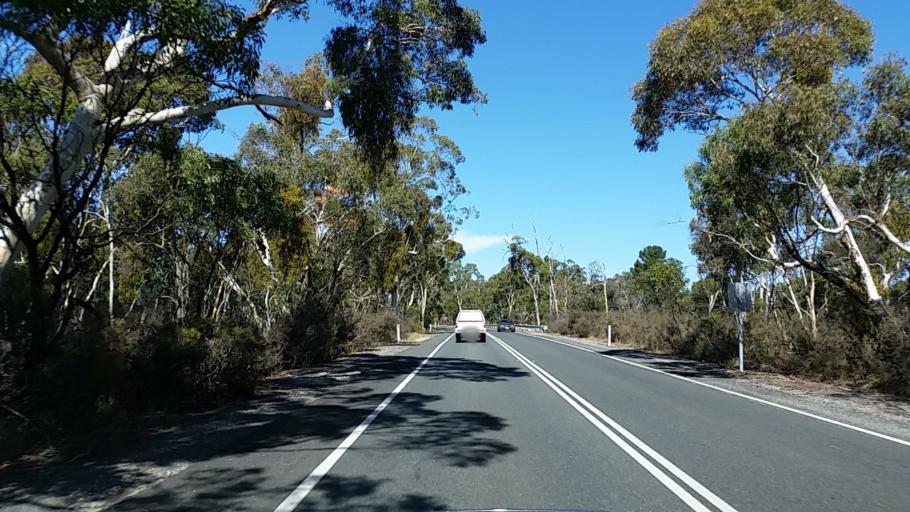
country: AU
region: South Australia
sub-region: Adelaide Hills
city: Birdwood
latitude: -34.7425
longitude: 138.9806
